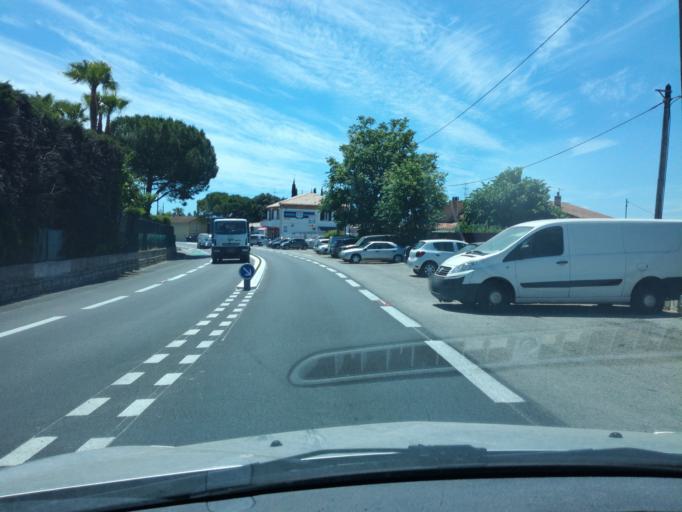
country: FR
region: Provence-Alpes-Cote d'Azur
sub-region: Departement des Alpes-Maritimes
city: Mougins
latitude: 43.5936
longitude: 7.0015
